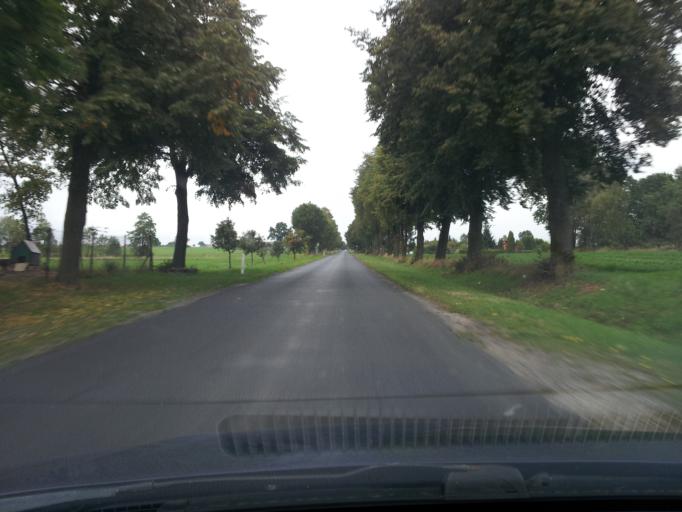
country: PL
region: Kujawsko-Pomorskie
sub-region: Powiat lipnowski
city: Lipno
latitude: 52.8220
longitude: 19.1838
